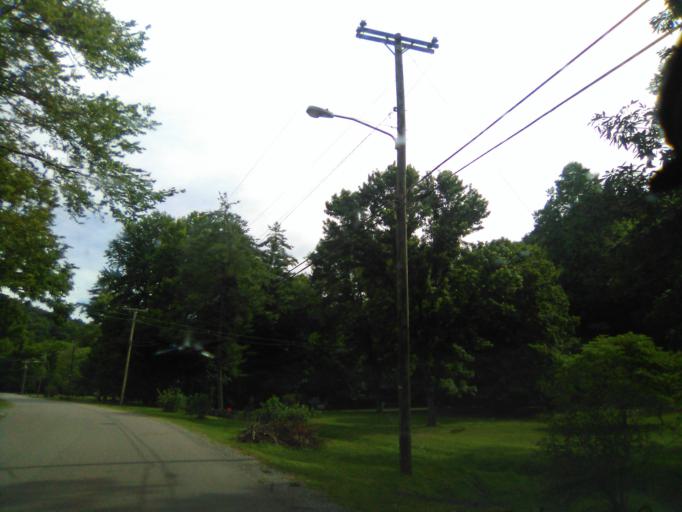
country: US
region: Tennessee
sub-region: Davidson County
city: Belle Meade
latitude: 36.0991
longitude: -86.9021
